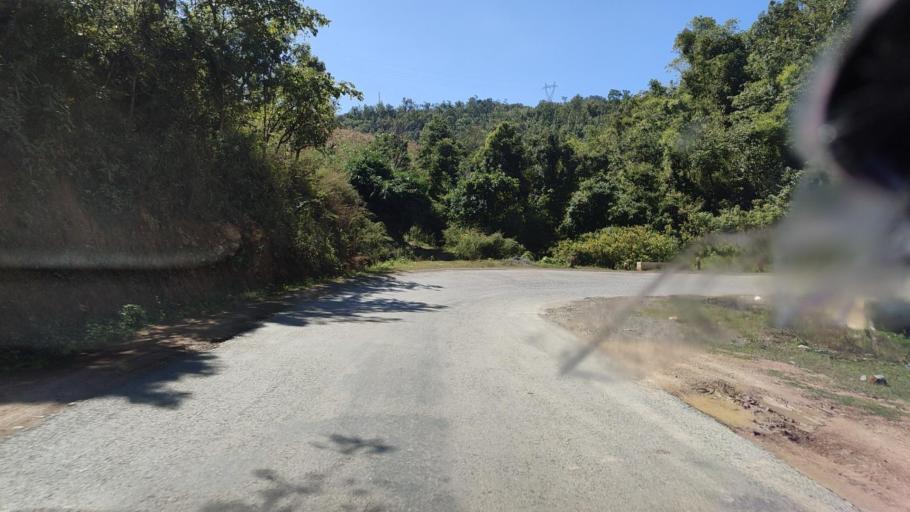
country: MM
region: Shan
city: Taunggyi
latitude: 20.8274
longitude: 97.3654
